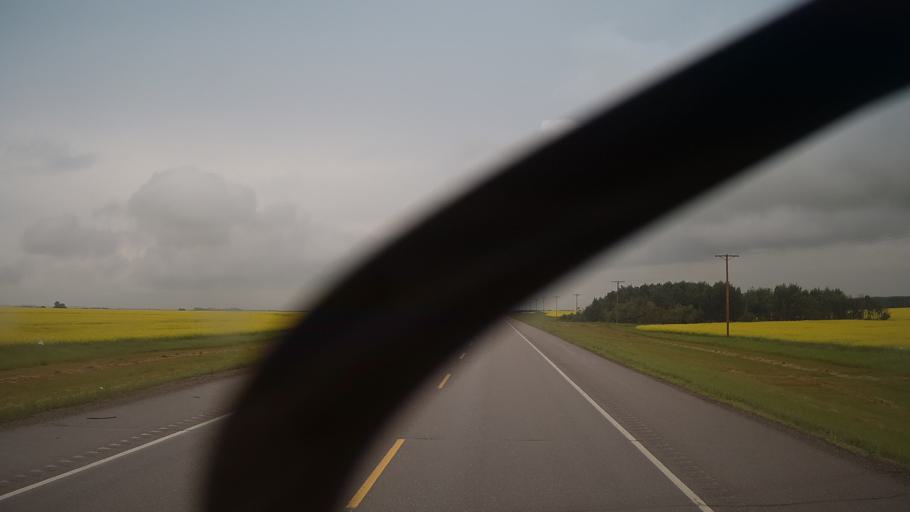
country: CA
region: Saskatchewan
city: Wilkie
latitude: 52.4259
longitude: -108.9083
